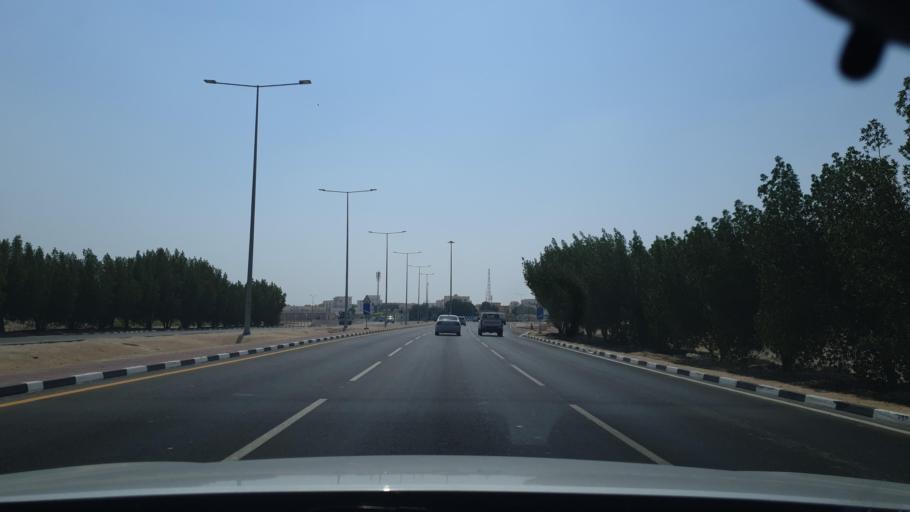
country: QA
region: Al Khawr
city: Al Khawr
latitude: 25.6931
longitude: 51.5008
